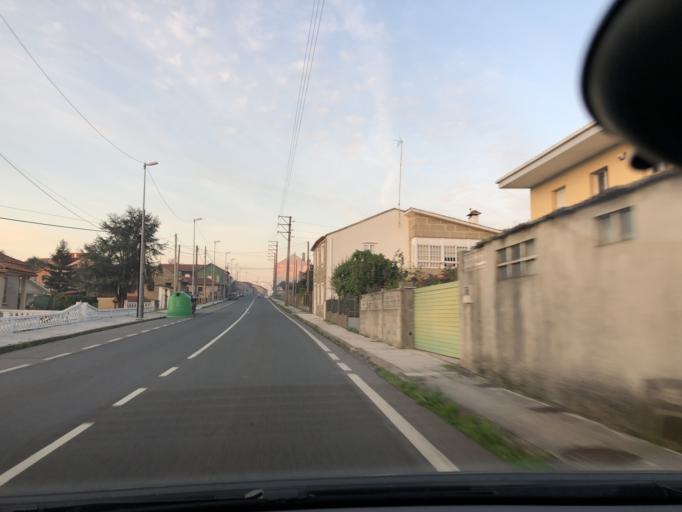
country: ES
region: Galicia
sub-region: Provincia de Pontevedra
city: Marin
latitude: 42.3840
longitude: -8.7139
